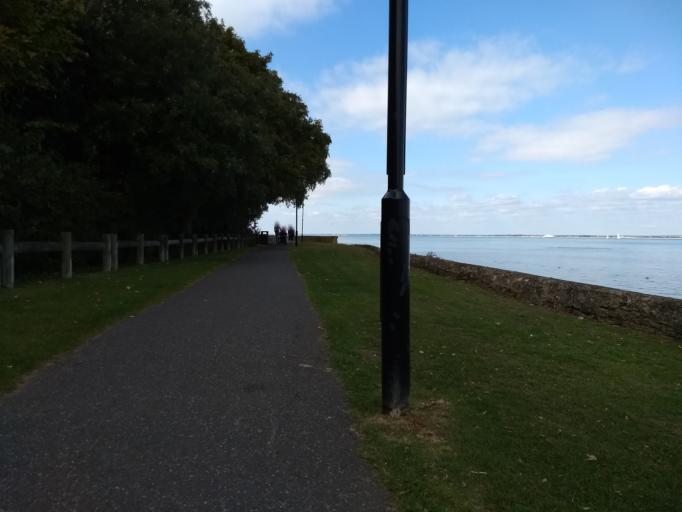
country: GB
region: England
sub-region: Isle of Wight
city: Seaview
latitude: 50.7260
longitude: -1.1285
